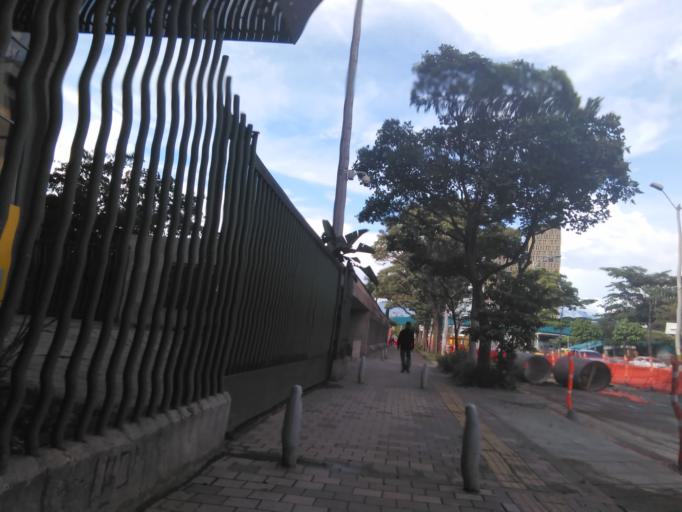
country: CO
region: Antioquia
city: Medellin
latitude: 6.2413
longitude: -75.5756
